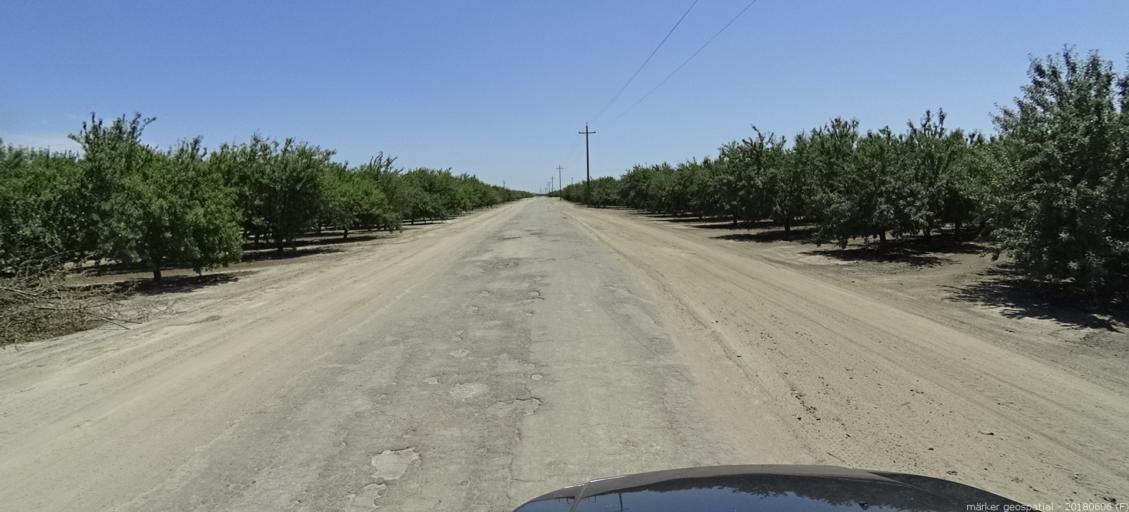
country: US
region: California
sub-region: Fresno County
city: Mendota
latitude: 36.7964
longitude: -120.3286
